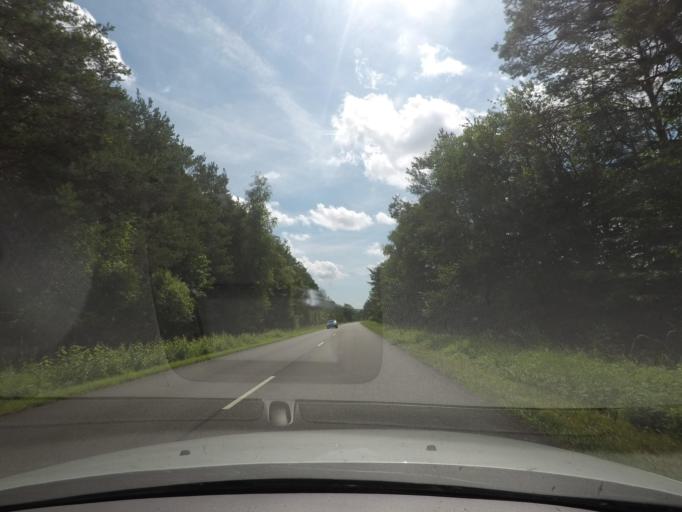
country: FR
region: Alsace
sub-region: Departement du Bas-Rhin
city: Drulingen
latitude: 48.8714
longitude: 7.1678
